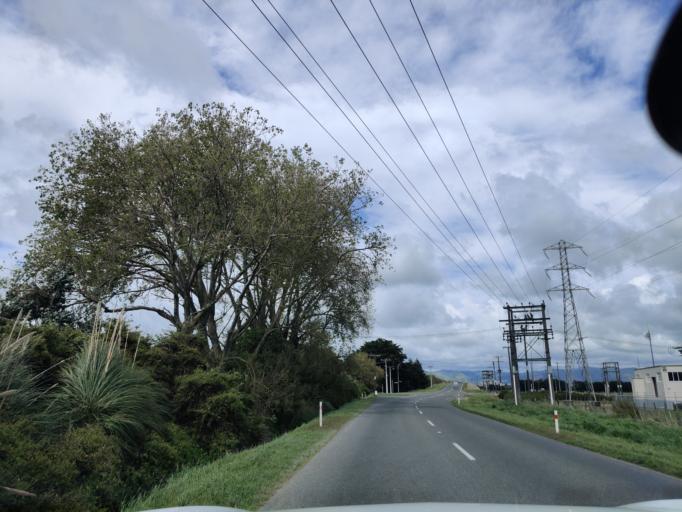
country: NZ
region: Manawatu-Wanganui
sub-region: Palmerston North City
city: Palmerston North
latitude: -40.3645
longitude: 175.5508
